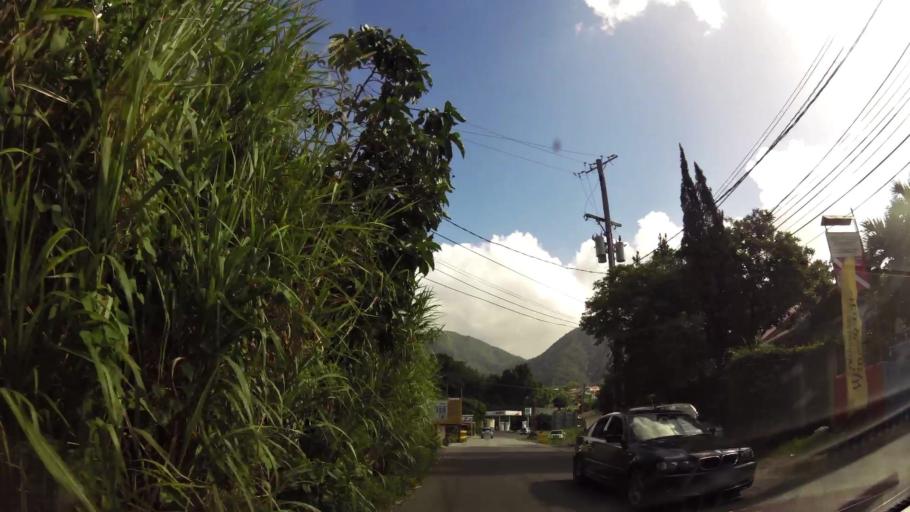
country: DM
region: Saint George
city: Roseau
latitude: 15.2856
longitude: -61.3752
